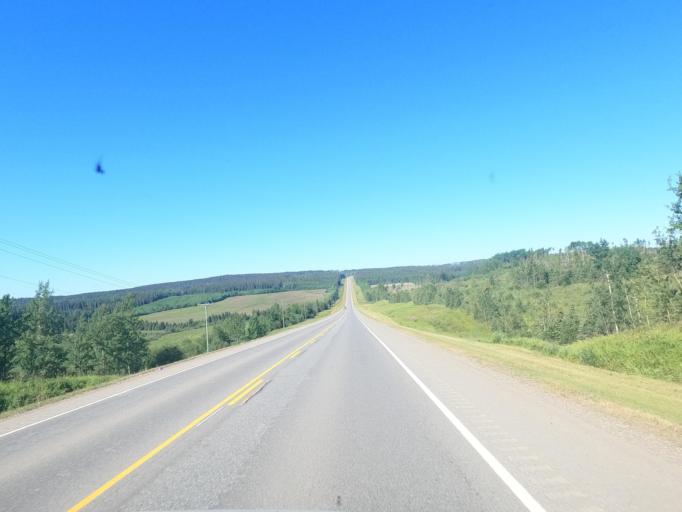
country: CA
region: British Columbia
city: Fort St. John
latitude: 56.6297
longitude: -121.5317
